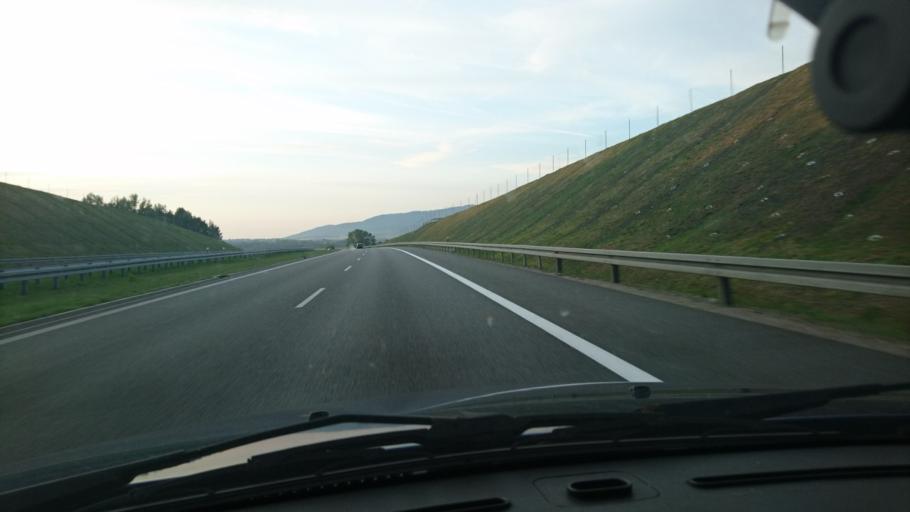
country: PL
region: Silesian Voivodeship
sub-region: Powiat zywiecki
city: Pietrzykowice
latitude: 49.6931
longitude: 19.1363
